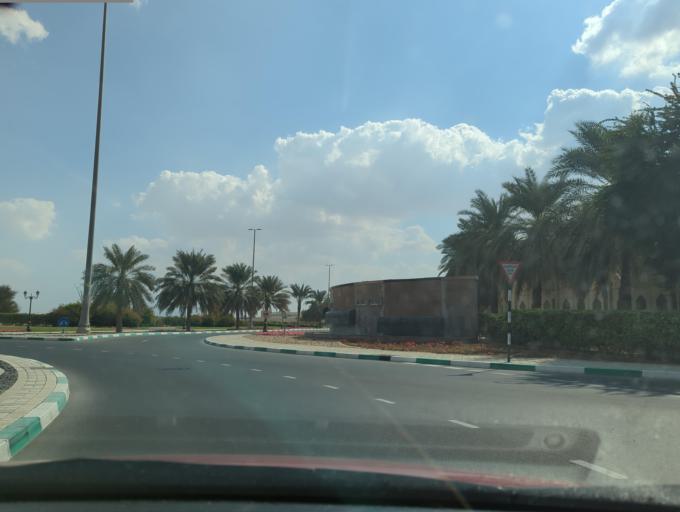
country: AE
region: Abu Dhabi
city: Al Ain
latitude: 24.1851
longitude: 55.6370
